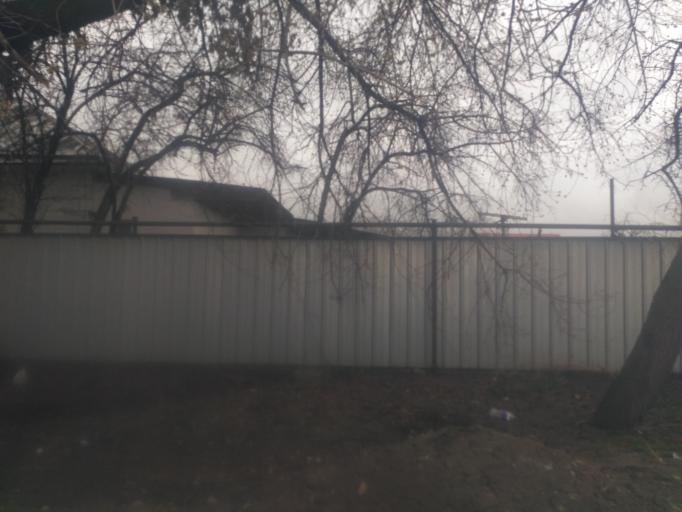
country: KZ
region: Almaty Qalasy
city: Almaty
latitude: 43.2192
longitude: 76.7645
